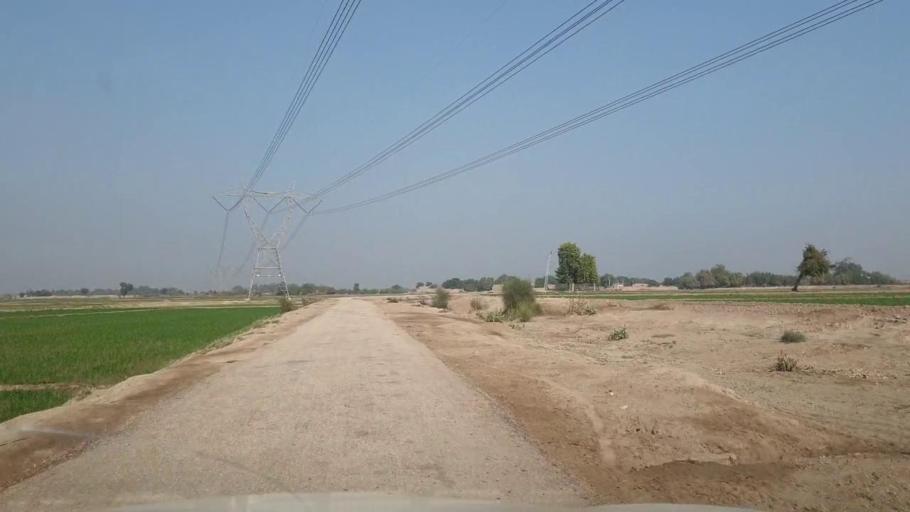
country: PK
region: Sindh
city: Bhan
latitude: 26.5445
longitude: 67.7484
